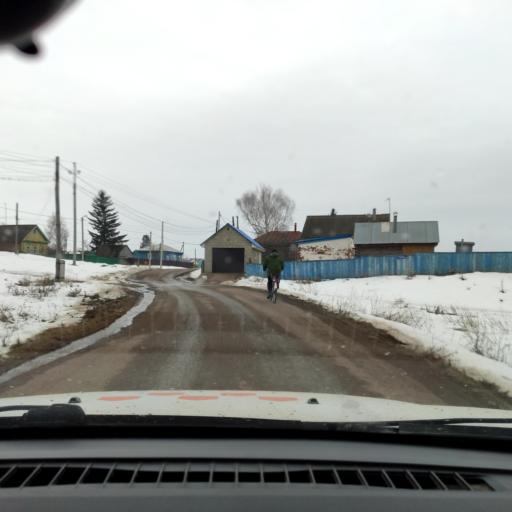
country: RU
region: Bashkortostan
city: Kushnarenkovo
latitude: 55.1120
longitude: 55.3386
